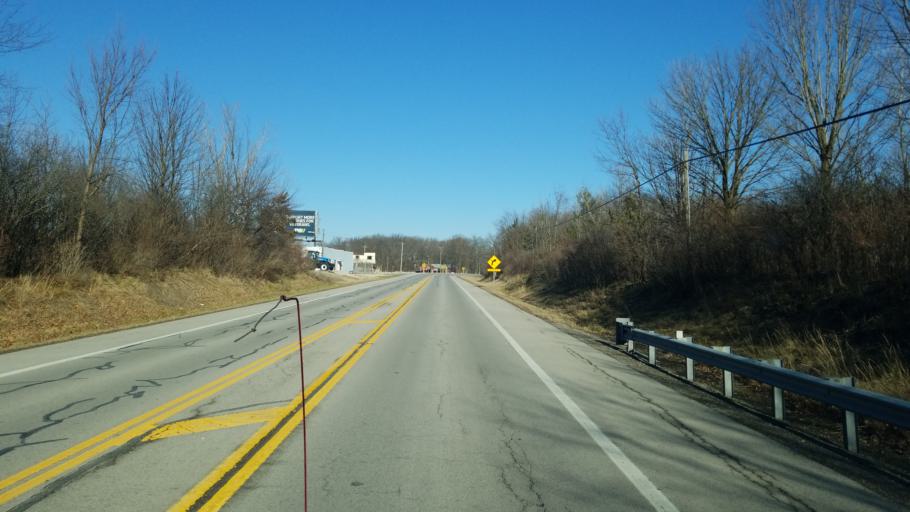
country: US
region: Ohio
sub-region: Wood County
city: Weston
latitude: 41.4213
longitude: -83.8550
